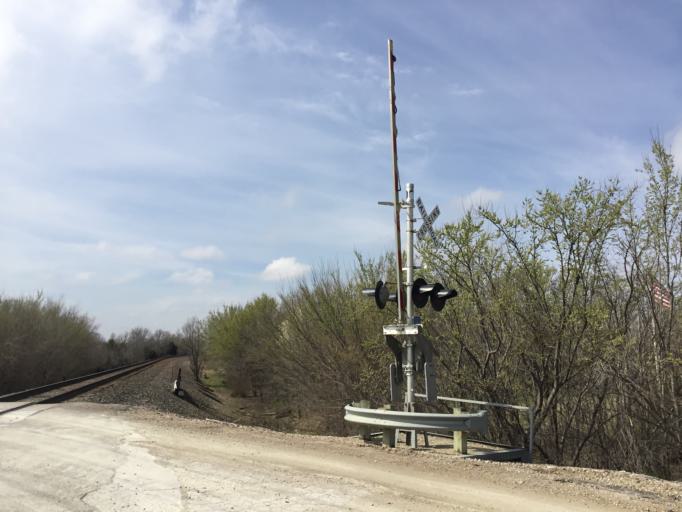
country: US
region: Kansas
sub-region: Butler County
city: Rose Hill
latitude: 37.5741
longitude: -97.1168
